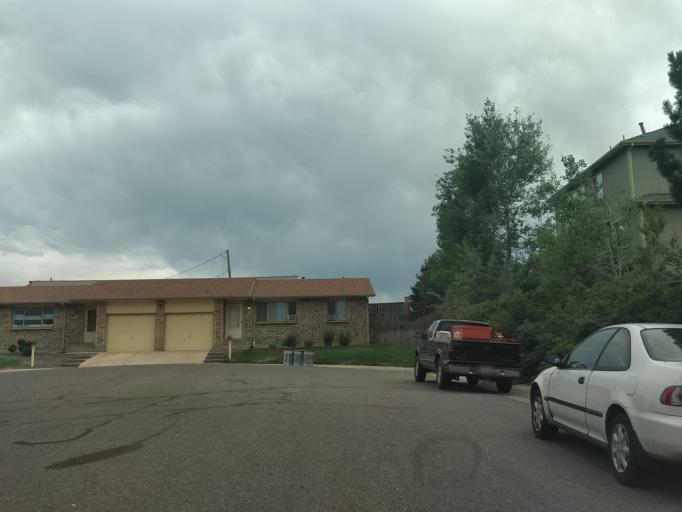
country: US
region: Colorado
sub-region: Jefferson County
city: Lakewood
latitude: 39.6990
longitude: -105.0851
